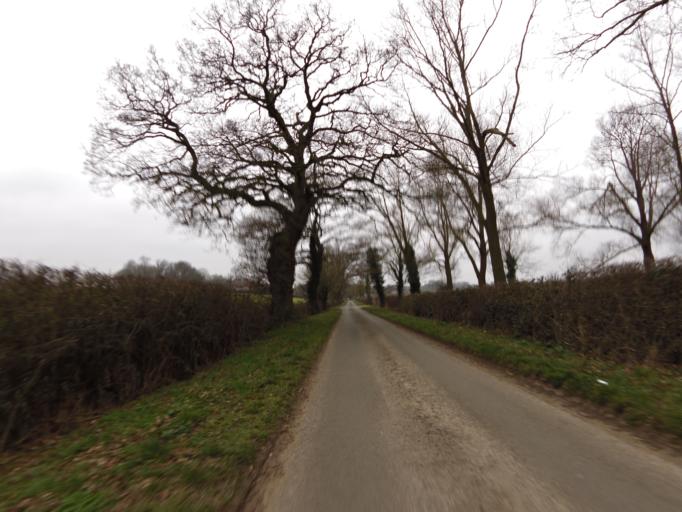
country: GB
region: England
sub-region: Suffolk
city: Framlingham
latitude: 52.2333
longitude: 1.3492
